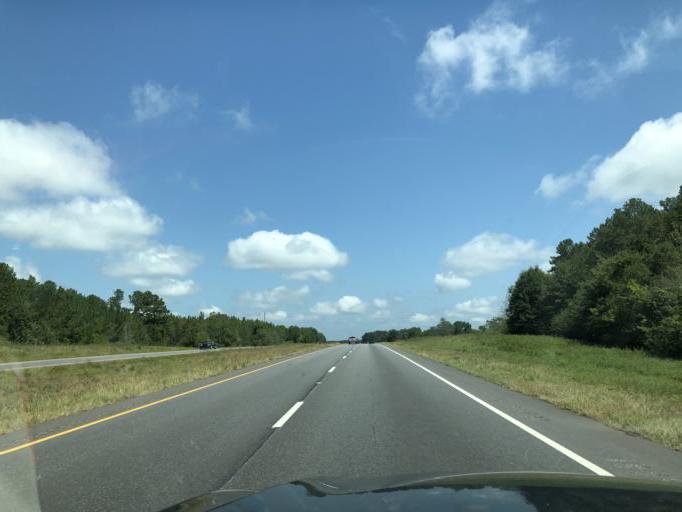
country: US
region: Alabama
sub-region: Henry County
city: Abbeville
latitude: 31.4951
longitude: -85.2948
